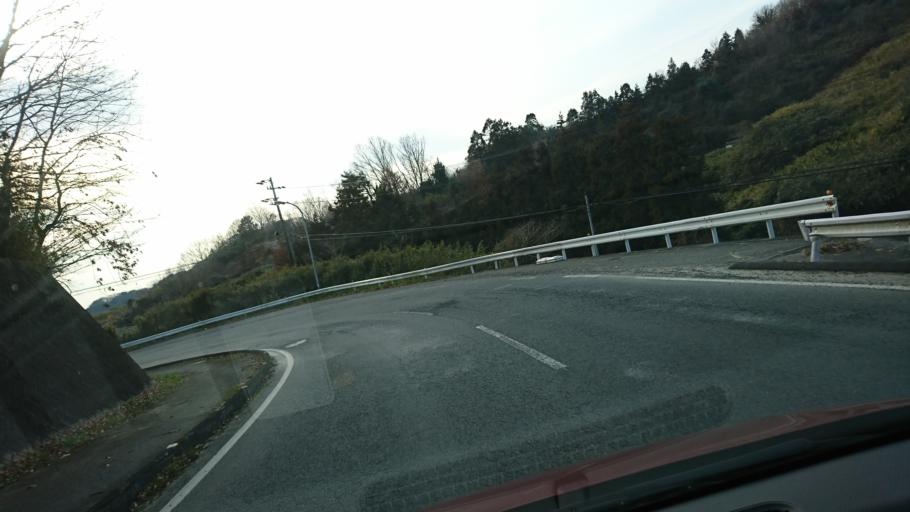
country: JP
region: Ehime
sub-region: Shikoku-chuo Shi
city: Matsuyama
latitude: 33.8981
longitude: 132.8057
